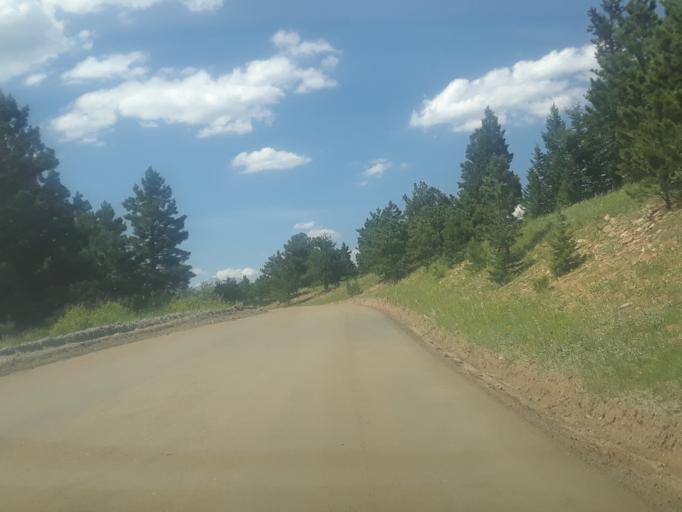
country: US
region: Colorado
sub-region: Boulder County
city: Nederland
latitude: 40.0516
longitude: -105.4725
